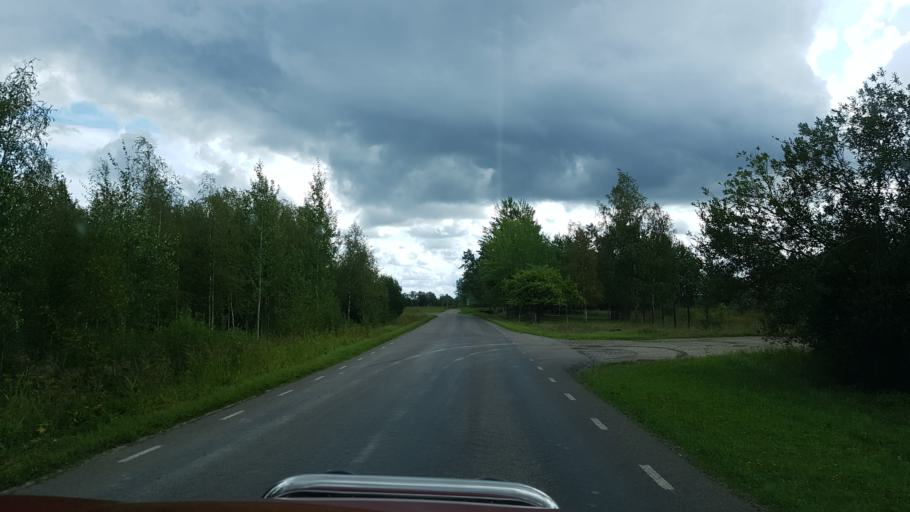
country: EE
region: Laeaene
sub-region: Lihula vald
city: Lihula
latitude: 58.7229
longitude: 23.9574
